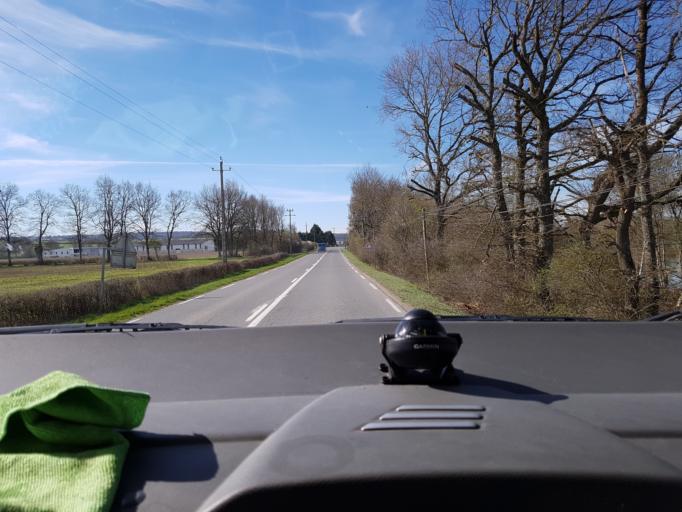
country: FR
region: Bourgogne
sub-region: Departement de Saone-et-Loire
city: Gueugnon
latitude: 46.5758
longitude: 4.0596
